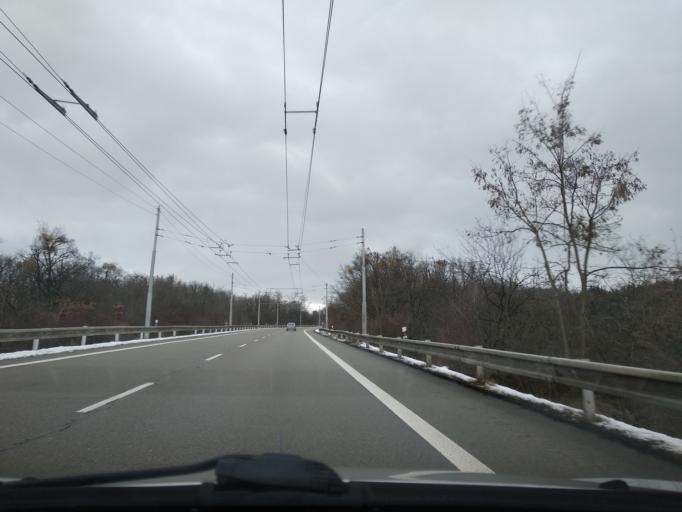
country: CZ
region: South Moravian
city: Ostopovice
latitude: 49.1795
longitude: 16.5452
